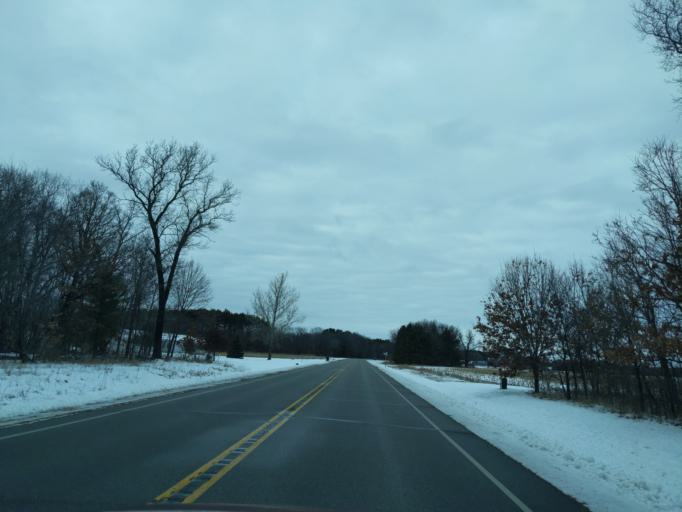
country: US
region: Wisconsin
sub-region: Waushara County
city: Wautoma
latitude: 43.9410
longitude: -89.3149
